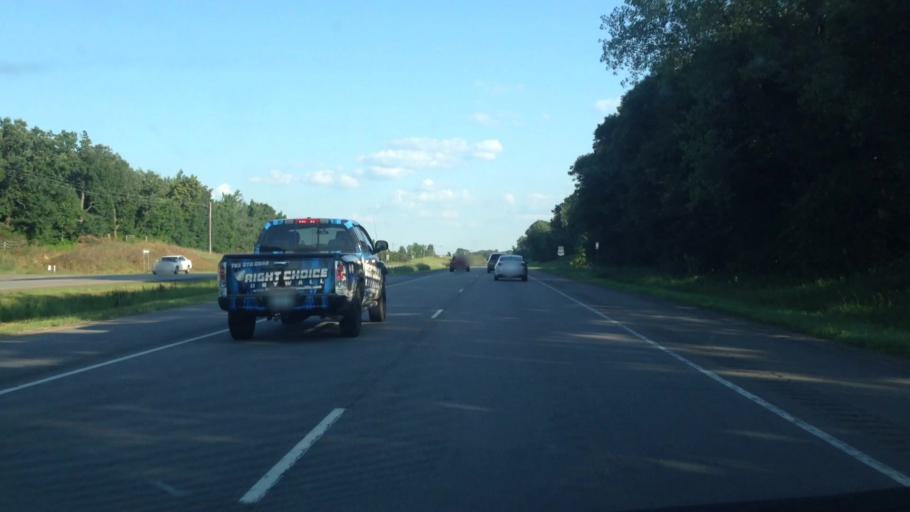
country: US
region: Minnesota
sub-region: Sherburne County
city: Zimmerman
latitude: 45.4005
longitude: -93.5654
